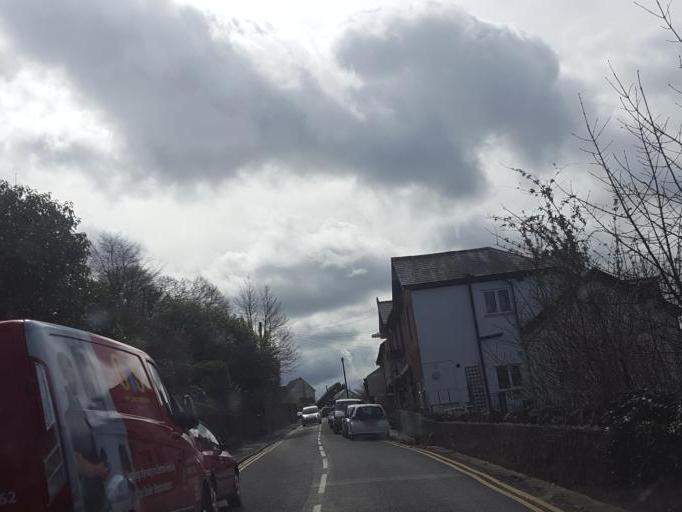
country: GB
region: England
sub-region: Worcestershire
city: Great Malvern
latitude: 52.1174
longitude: -2.3460
